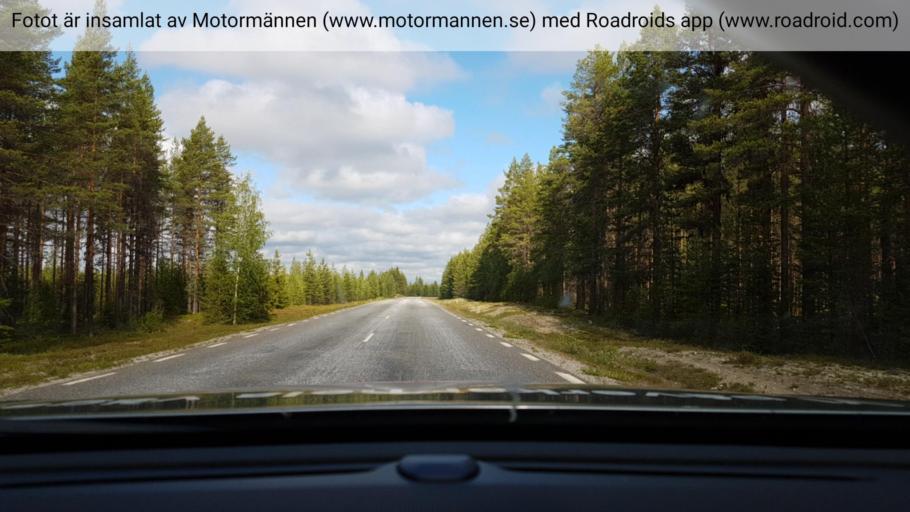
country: SE
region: Vaesterbotten
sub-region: Lycksele Kommun
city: Lycksele
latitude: 64.8040
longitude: 18.9458
